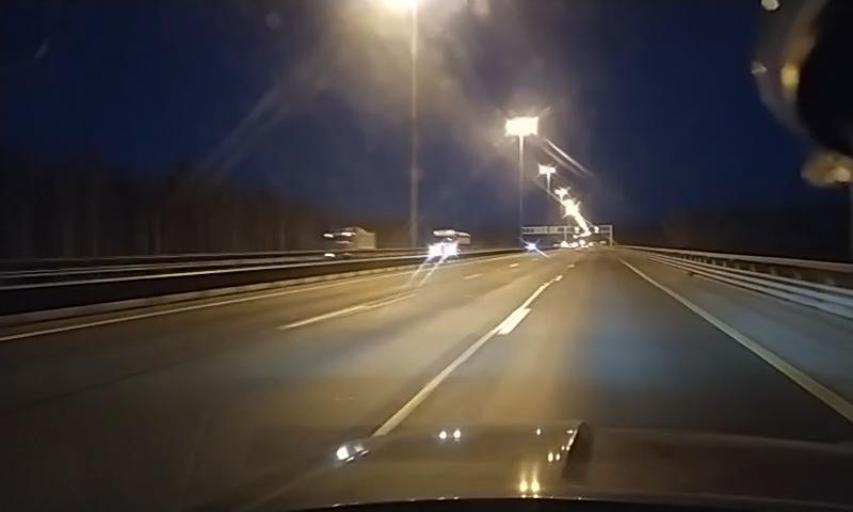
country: RU
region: St.-Petersburg
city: Pesochnyy
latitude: 60.1003
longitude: 30.0910
